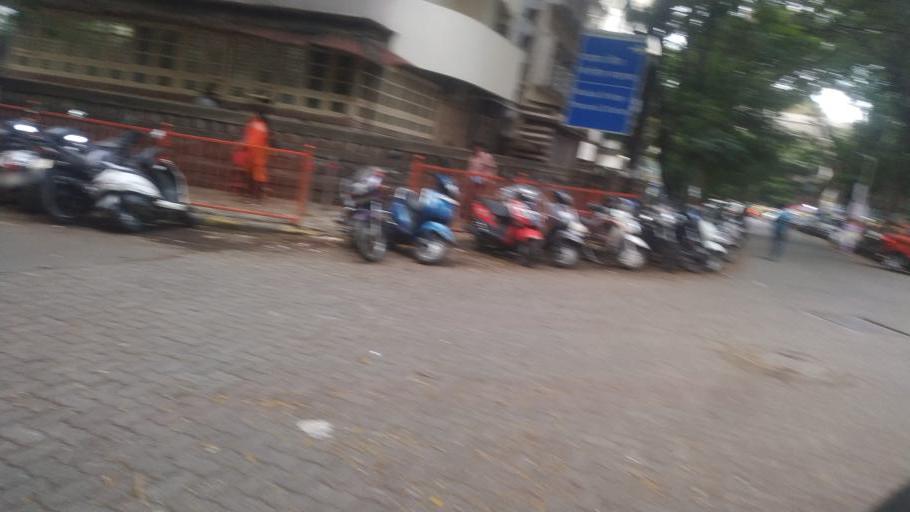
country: IN
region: Maharashtra
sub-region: Mumbai Suburban
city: Mumbai
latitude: 19.0168
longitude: 72.8574
